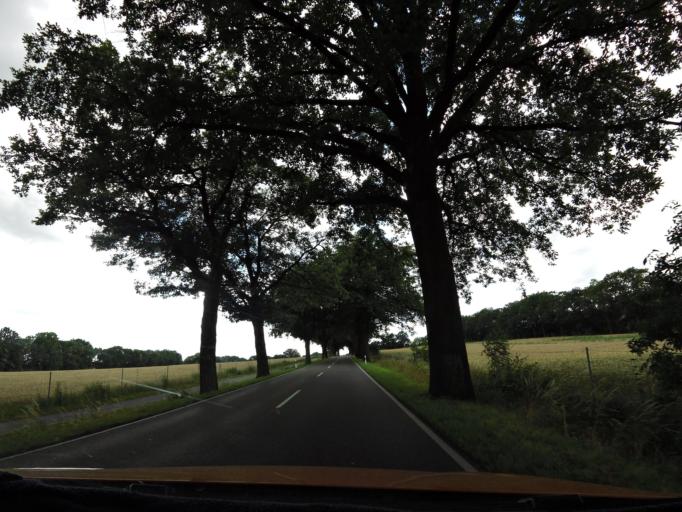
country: DE
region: Brandenburg
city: Mittenwalde
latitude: 52.2927
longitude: 13.5682
